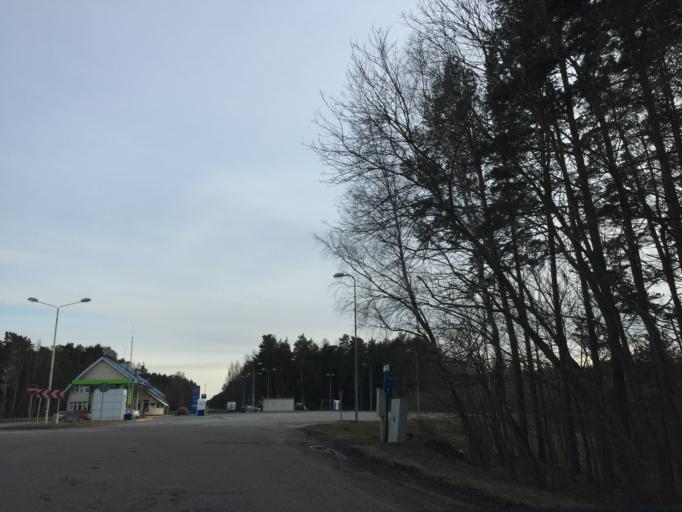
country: LV
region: Salacgrivas
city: Ainazi
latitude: 57.8507
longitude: 24.3538
